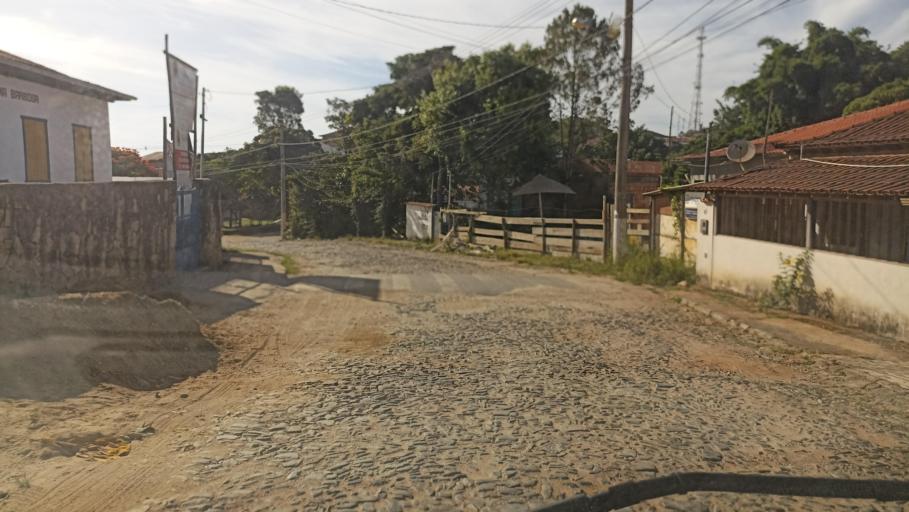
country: BR
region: Minas Gerais
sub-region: Tiradentes
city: Tiradentes
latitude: -21.1145
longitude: -44.1841
